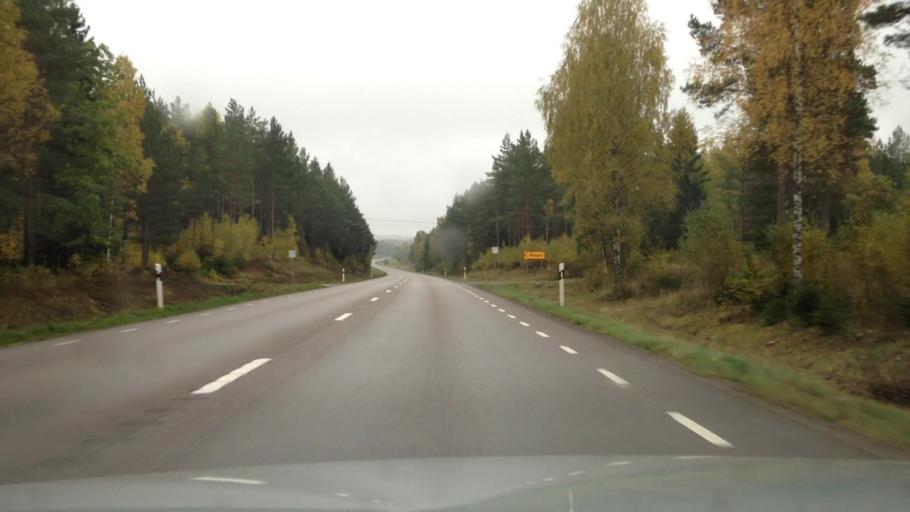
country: SE
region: Vaestra Goetaland
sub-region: Falkopings Kommun
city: Falkoeping
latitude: 58.2572
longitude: 13.5027
